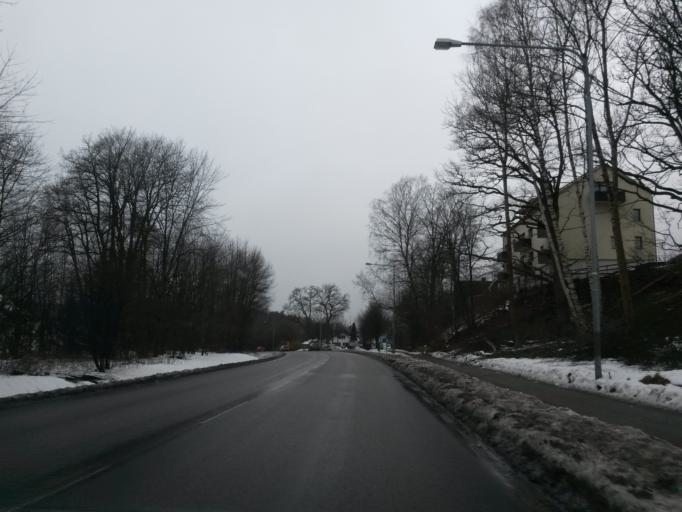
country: SE
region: Vaestra Goetaland
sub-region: Boras Kommun
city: Boras
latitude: 57.7063
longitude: 12.9575
